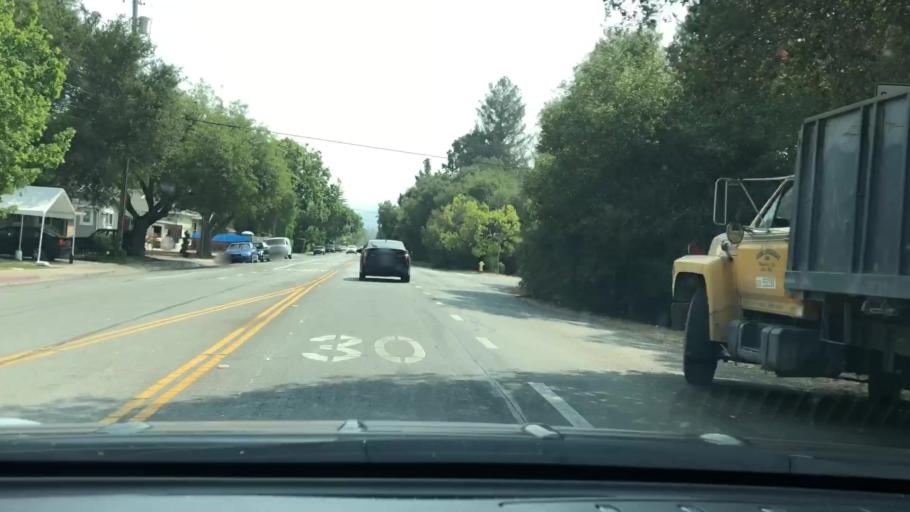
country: US
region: California
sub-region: Santa Clara County
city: Mountain View
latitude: 37.3733
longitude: -122.0961
